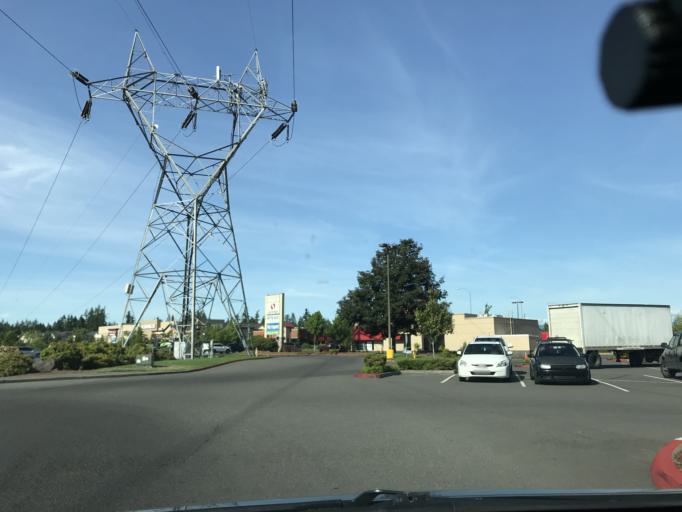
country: US
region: Washington
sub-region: King County
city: Covington
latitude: 47.3574
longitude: -122.1156
